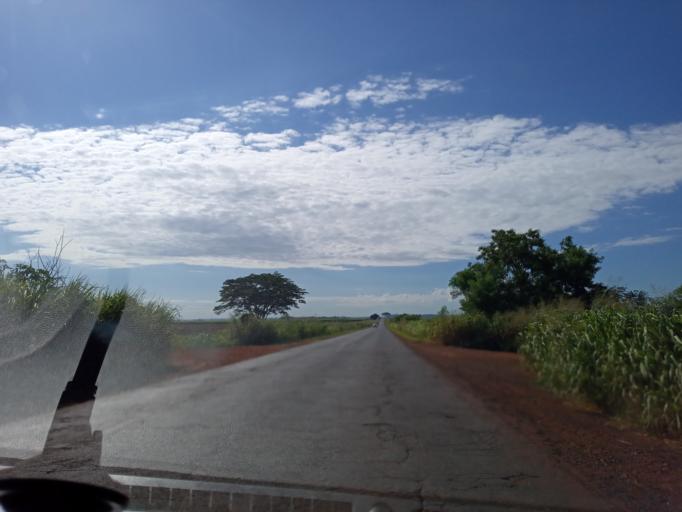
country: BR
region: Goias
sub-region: Itumbiara
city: Itumbiara
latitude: -18.4466
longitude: -49.1699
